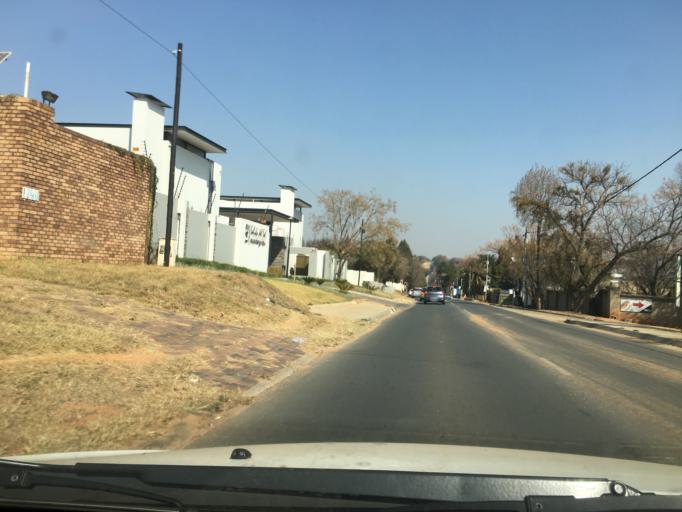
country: ZA
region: Gauteng
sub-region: City of Johannesburg Metropolitan Municipality
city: Midrand
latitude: -26.0632
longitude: 28.0545
